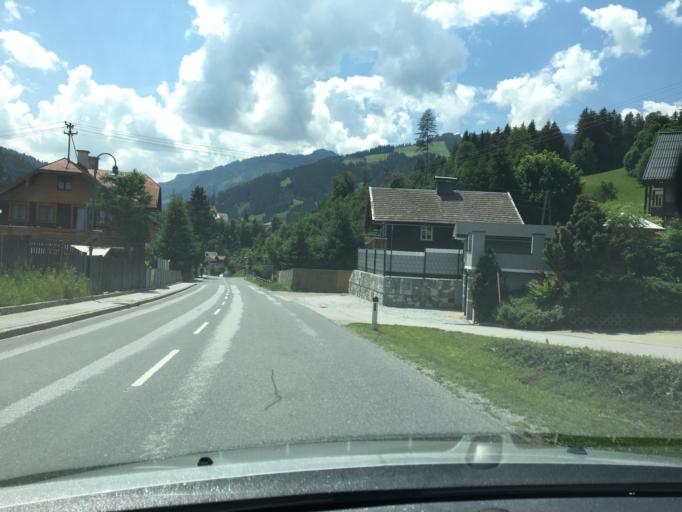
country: AT
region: Salzburg
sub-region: Politischer Bezirk Sankt Johann im Pongau
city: Wagrain
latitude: 47.3404
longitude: 13.3044
